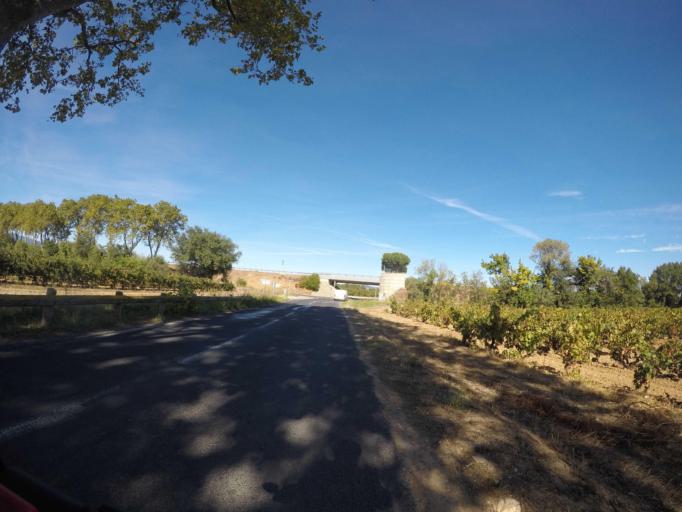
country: FR
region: Languedoc-Roussillon
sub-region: Departement des Pyrenees-Orientales
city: Le Soler
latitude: 42.6528
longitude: 2.7955
